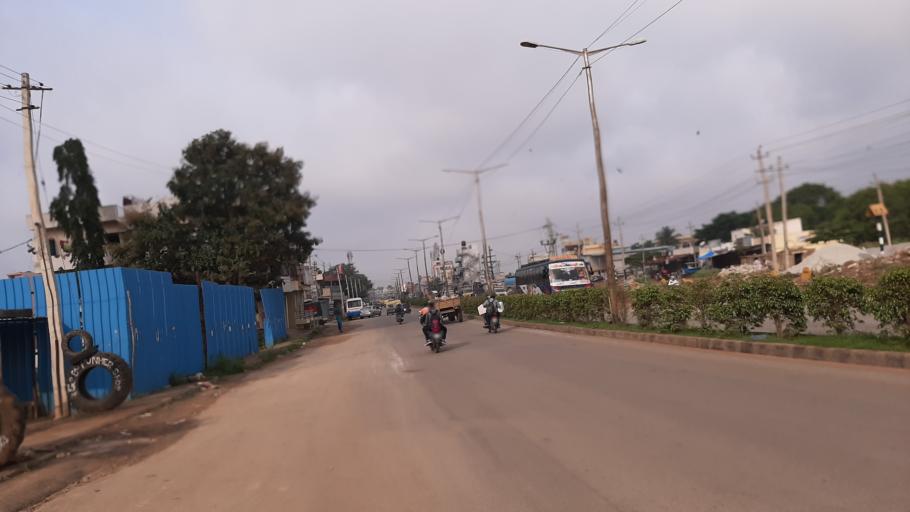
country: IN
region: Karnataka
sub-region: Bangalore Urban
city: Bangalore
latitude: 12.9866
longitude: 77.4903
